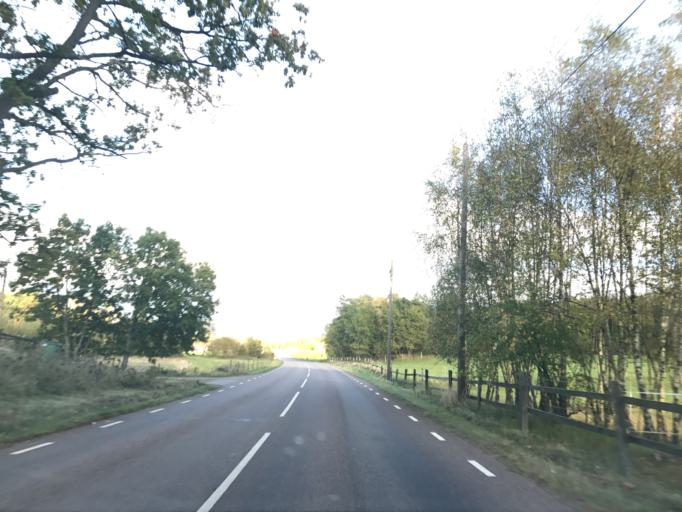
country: SE
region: Skane
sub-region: Klippans Kommun
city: Ljungbyhed
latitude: 56.1386
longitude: 13.2365
